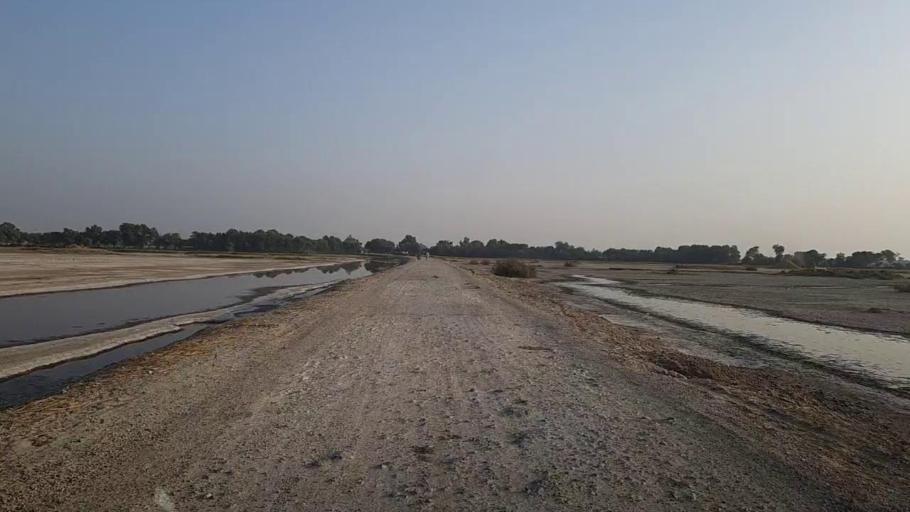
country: PK
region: Sindh
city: Kandhkot
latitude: 28.2448
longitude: 69.0911
